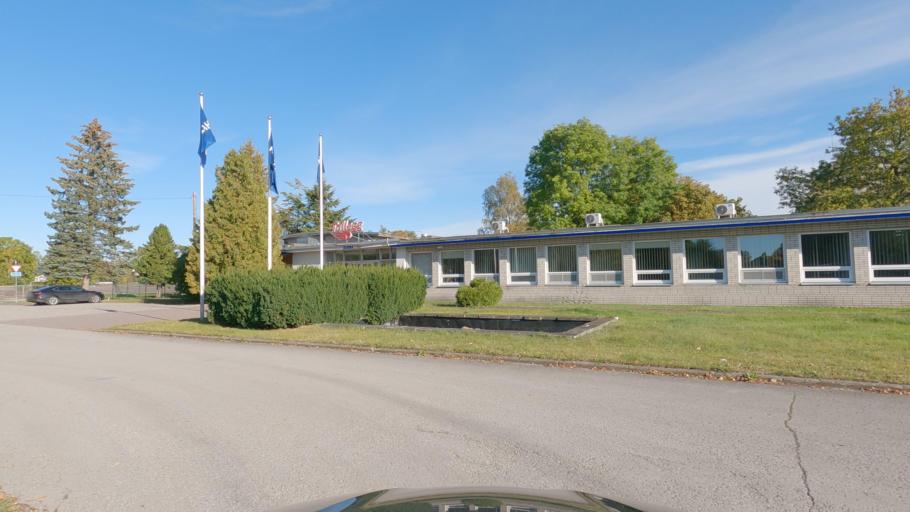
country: EE
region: Harju
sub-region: Joelaehtme vald
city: Loo
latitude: 59.4315
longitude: 24.9515
